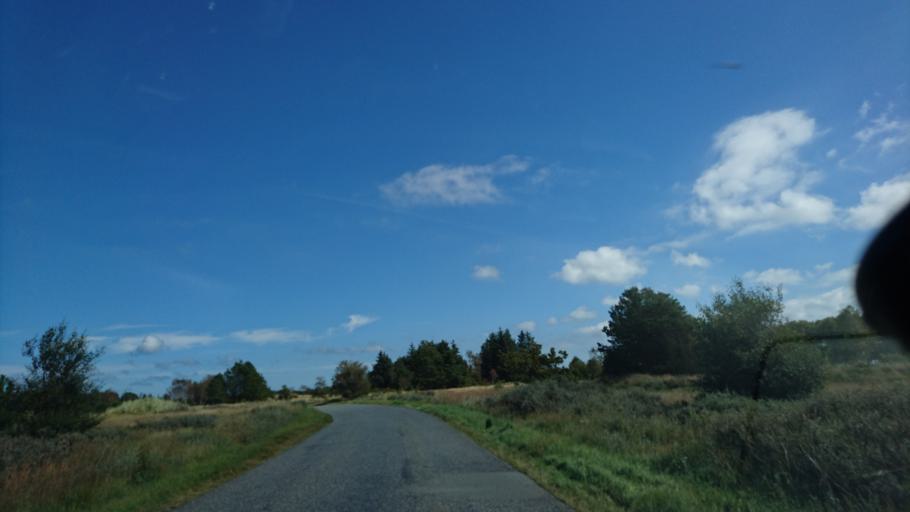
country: DK
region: North Denmark
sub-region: Frederikshavn Kommune
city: Strandby
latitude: 57.6256
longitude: 10.3858
